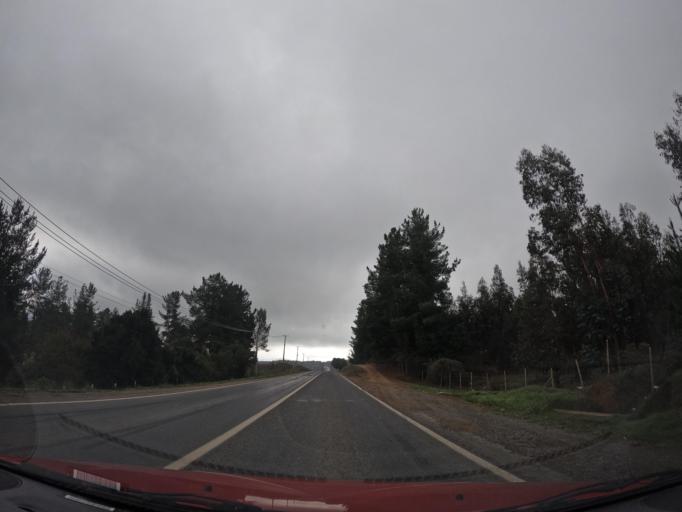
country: CL
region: Maule
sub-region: Provincia de Cauquenes
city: Cauquenes
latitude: -36.2480
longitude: -72.5484
